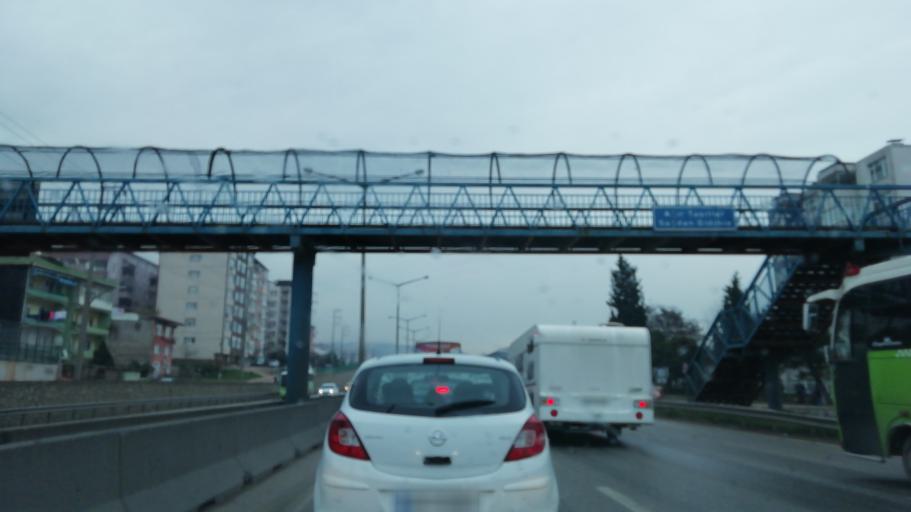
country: TR
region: Kocaeli
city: Izmit
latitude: 40.7636
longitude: 29.8903
